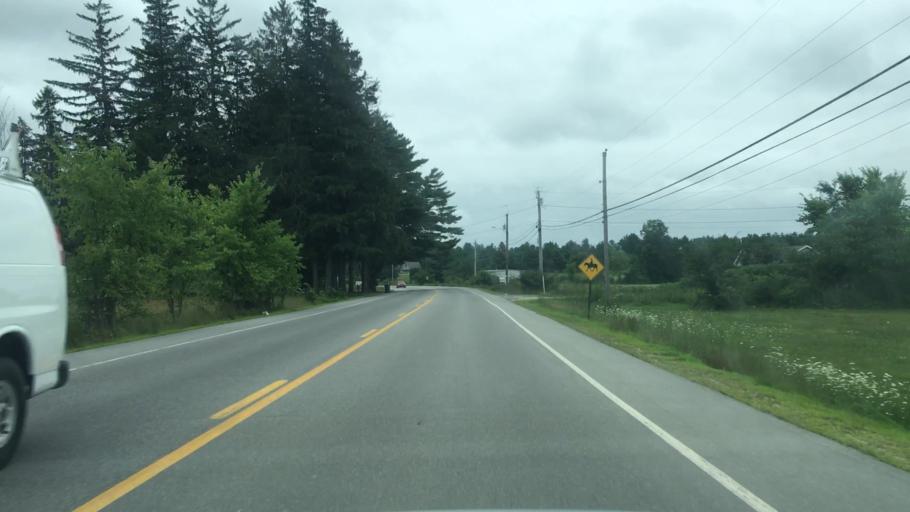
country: US
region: Maine
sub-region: York County
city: Biddeford
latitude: 43.5186
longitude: -70.4815
